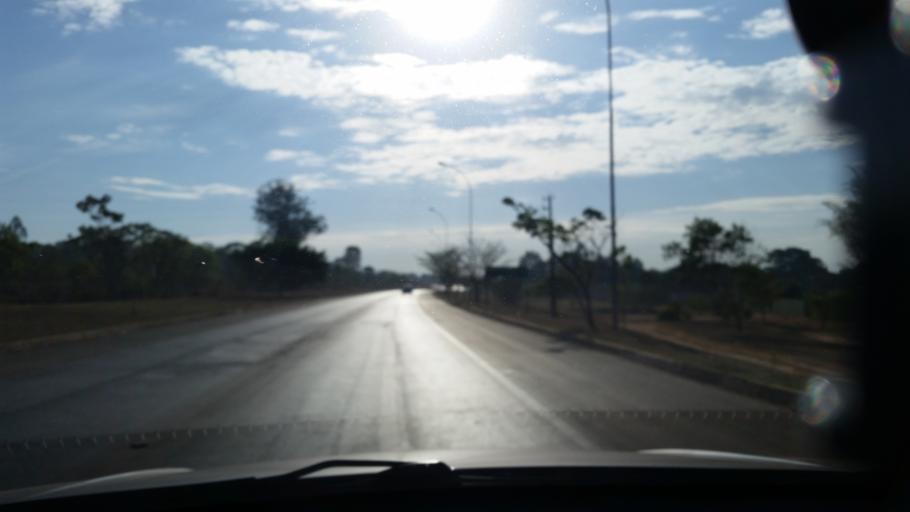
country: BR
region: Federal District
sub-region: Brasilia
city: Brasilia
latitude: -15.7245
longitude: -47.9030
